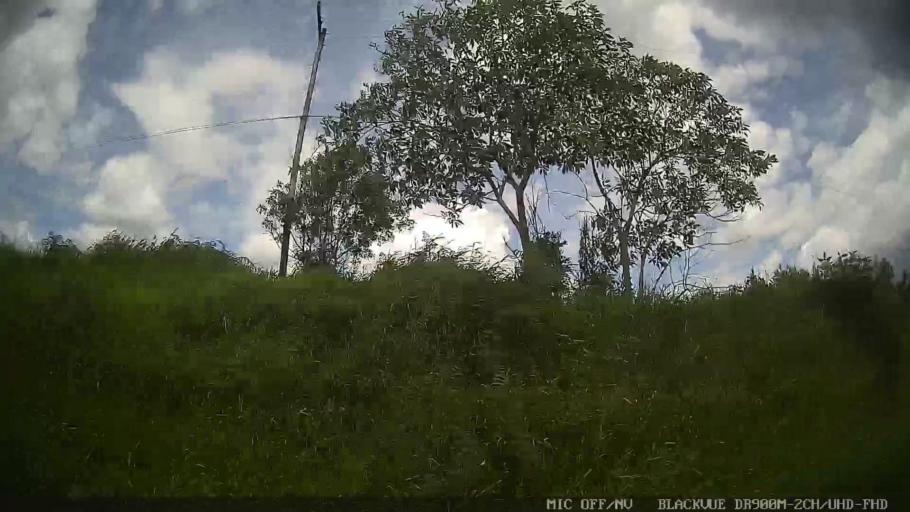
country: BR
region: Sao Paulo
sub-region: Rio Grande Da Serra
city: Rio Grande da Serra
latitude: -23.6870
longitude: -46.2601
